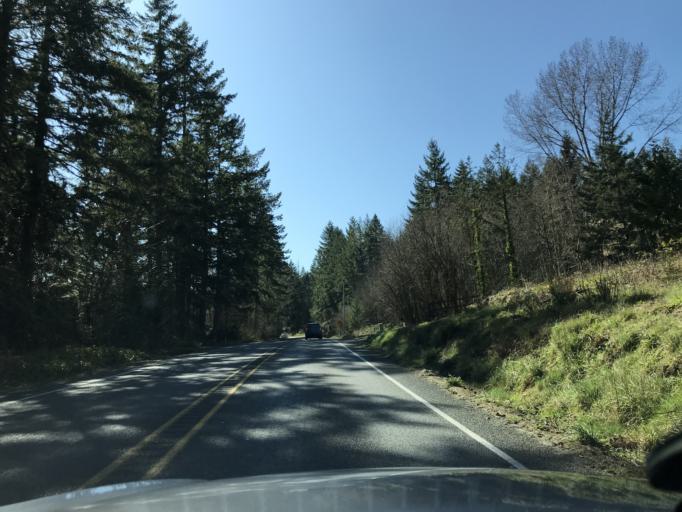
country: US
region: Washington
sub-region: Pierce County
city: Key Center
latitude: 47.3486
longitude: -122.7391
